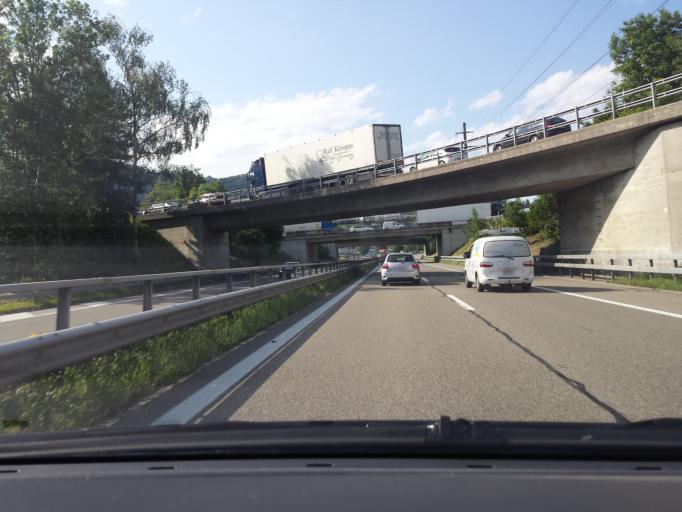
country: CH
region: Saint Gallen
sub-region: Wahlkreis Rheintal
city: Au
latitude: 47.4299
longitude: 9.6439
